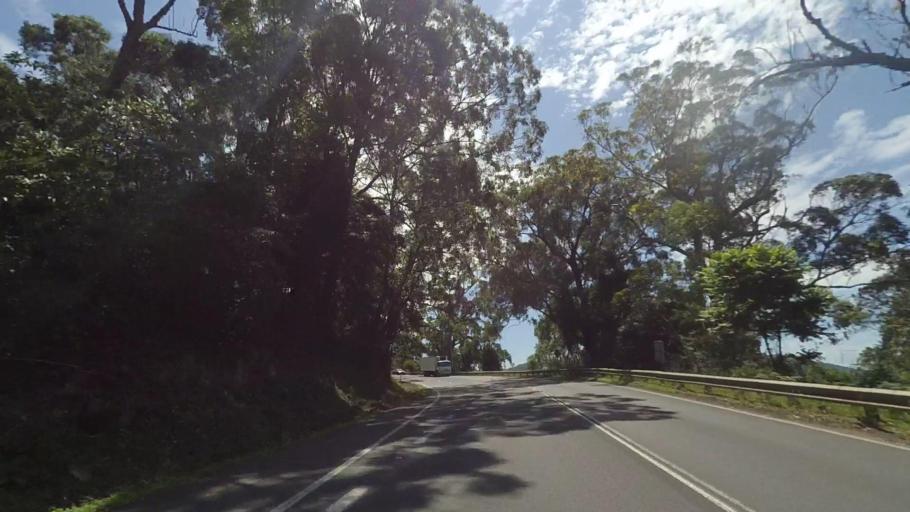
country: AU
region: New South Wales
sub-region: Kiama
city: Gerringong
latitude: -34.7452
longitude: 150.7734
